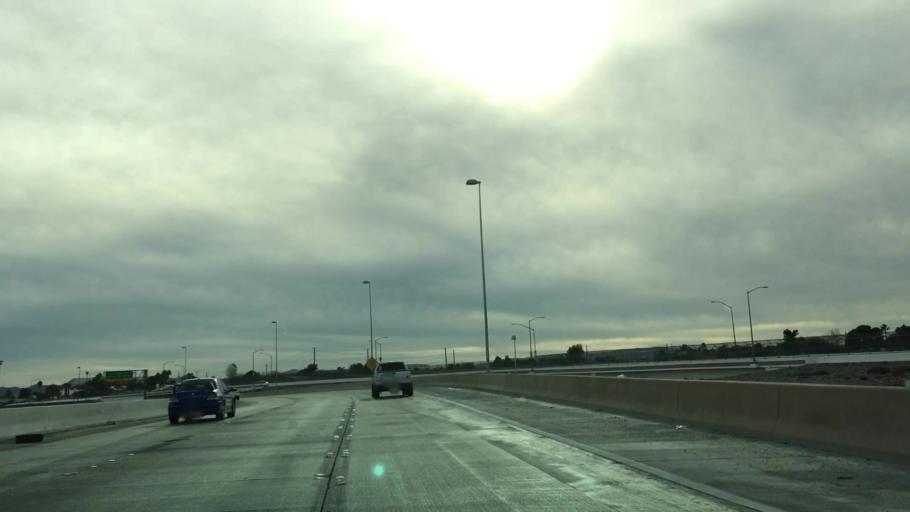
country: US
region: Nevada
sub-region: Clark County
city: Paradise
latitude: 36.0656
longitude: -115.1830
